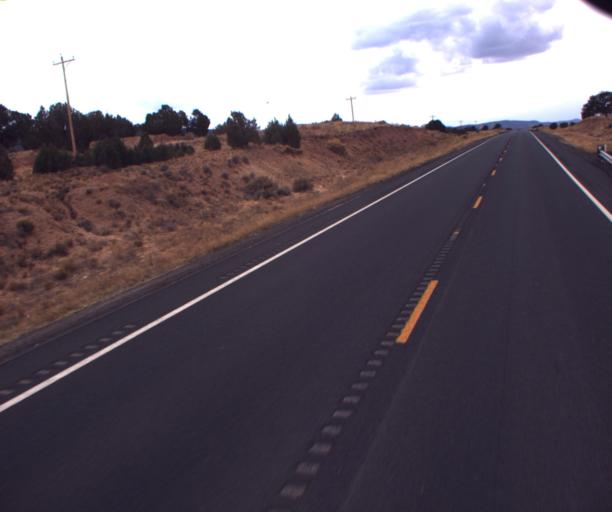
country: US
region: Arizona
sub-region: Navajo County
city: Kayenta
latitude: 36.4943
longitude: -110.6271
